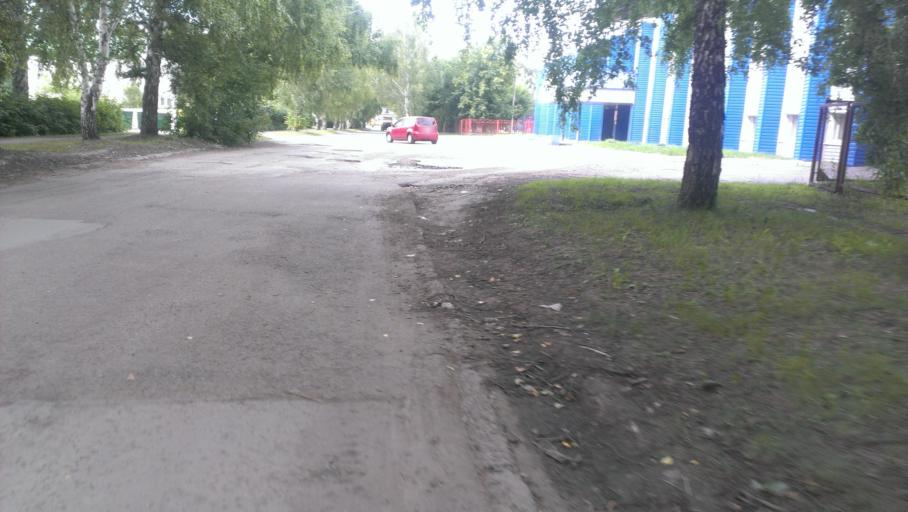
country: RU
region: Altai Krai
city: Yuzhnyy
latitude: 53.2520
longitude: 83.6925
